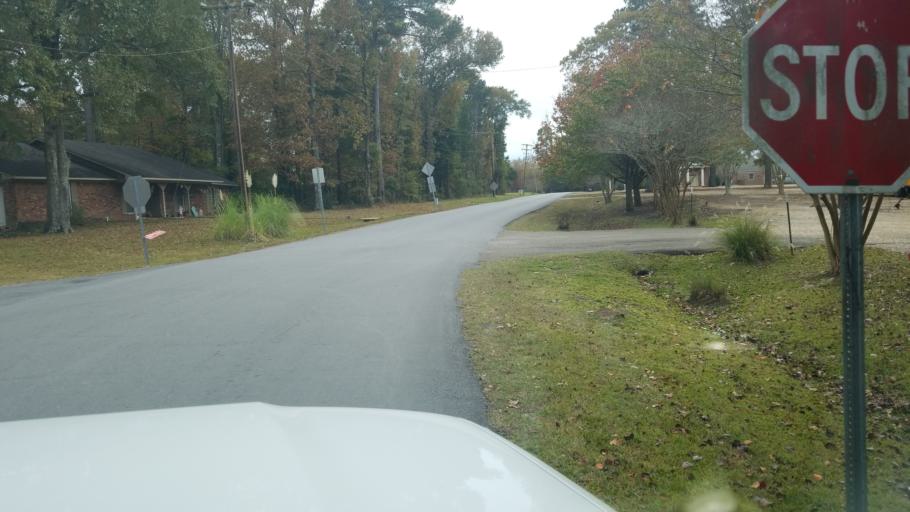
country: US
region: Mississippi
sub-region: Madison County
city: Ridgeland
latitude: 32.3810
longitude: -90.0318
